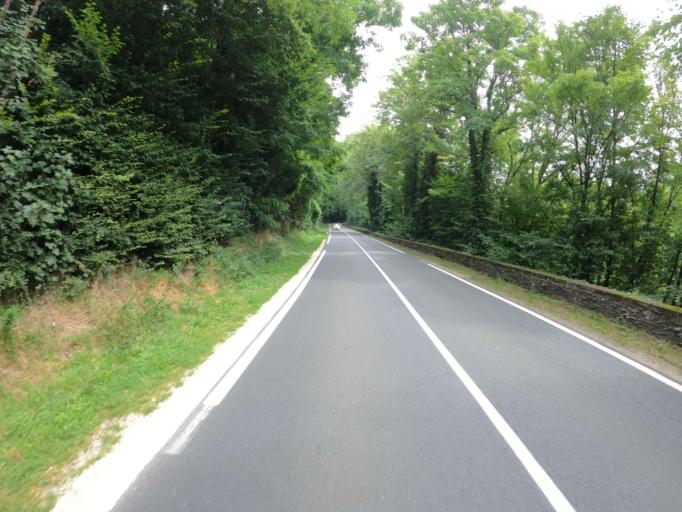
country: FR
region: Poitou-Charentes
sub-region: Departement de la Vienne
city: Savigne
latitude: 46.1587
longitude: 0.3257
